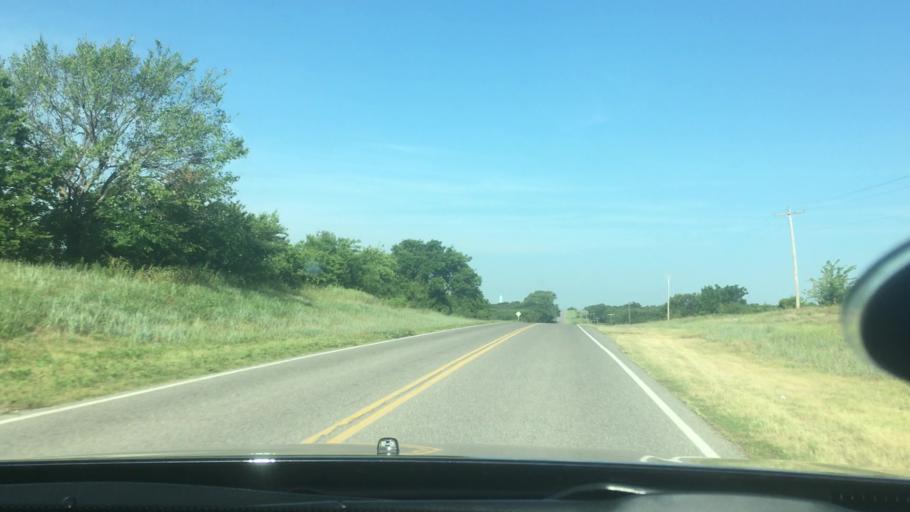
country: US
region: Oklahoma
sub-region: Garvin County
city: Pauls Valley
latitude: 34.6518
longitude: -97.2671
